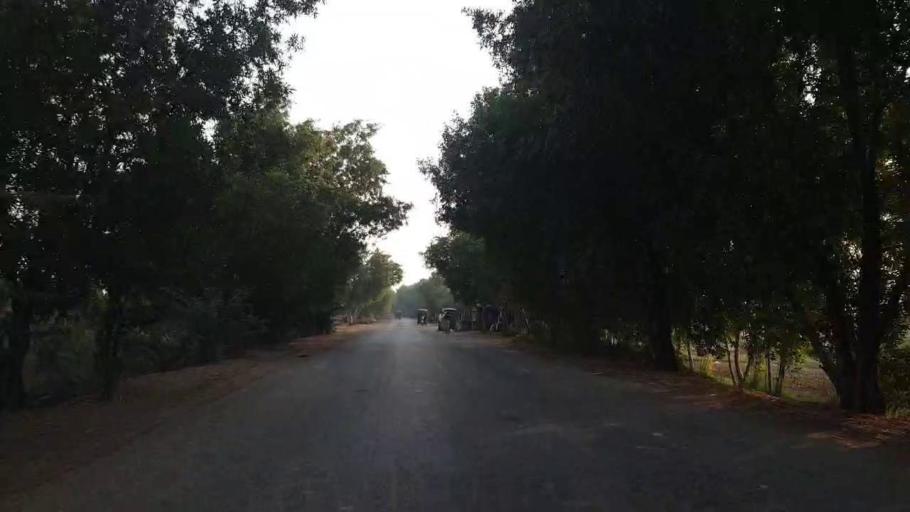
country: PK
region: Sindh
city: Badin
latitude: 24.6789
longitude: 68.9064
